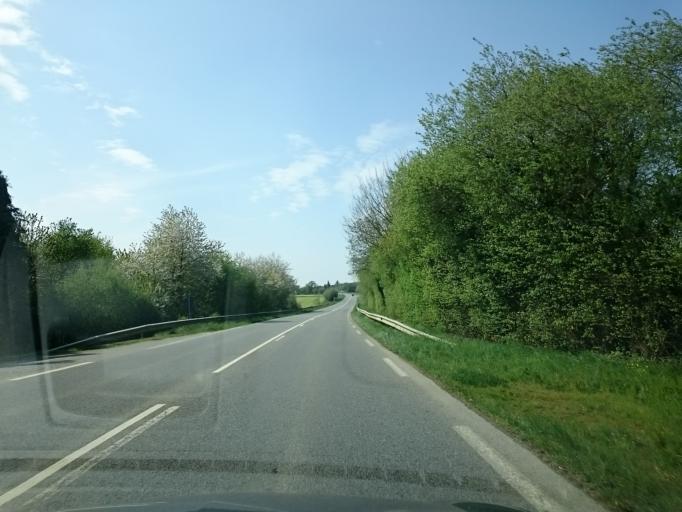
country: FR
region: Brittany
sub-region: Departement d'Ille-et-Vilaine
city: Nouvoitou
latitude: 48.0576
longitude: -1.5399
